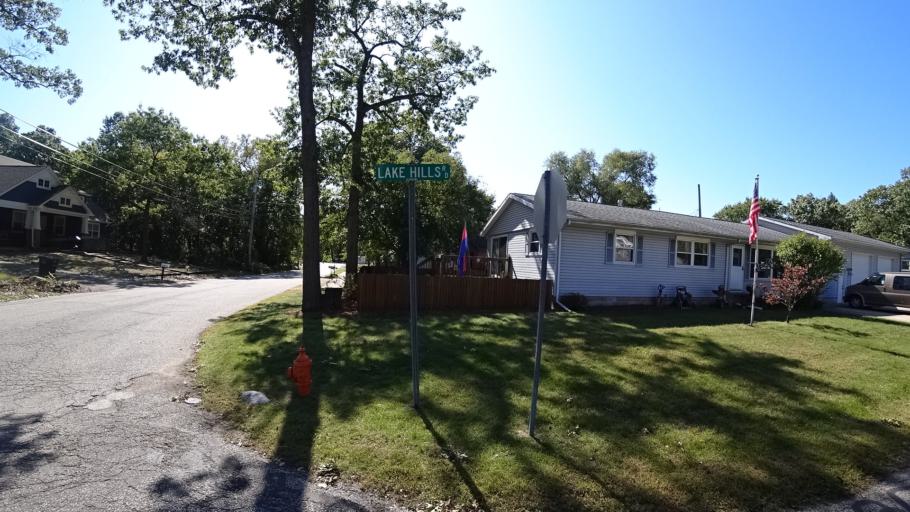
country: US
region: Indiana
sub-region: LaPorte County
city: Michigan City
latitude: 41.7275
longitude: -86.8805
